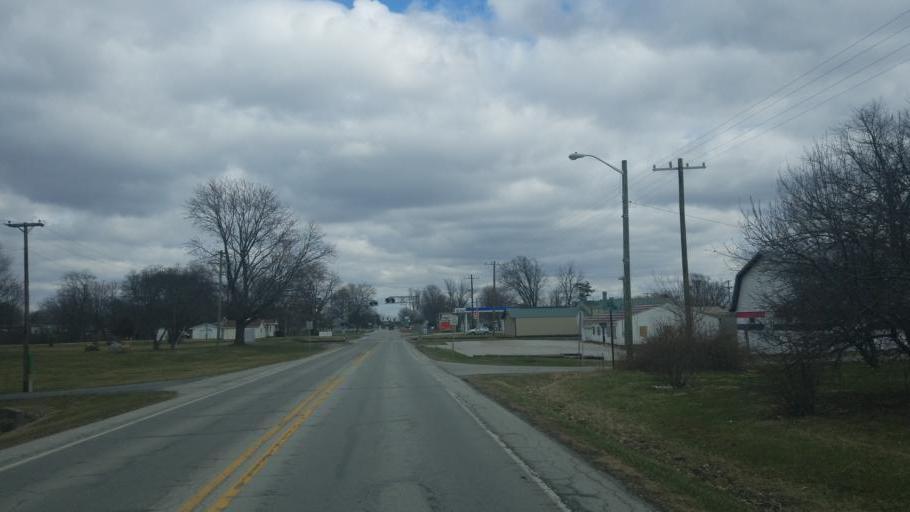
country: US
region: Indiana
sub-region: Putnam County
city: Greencastle
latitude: 39.7620
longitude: -86.8169
